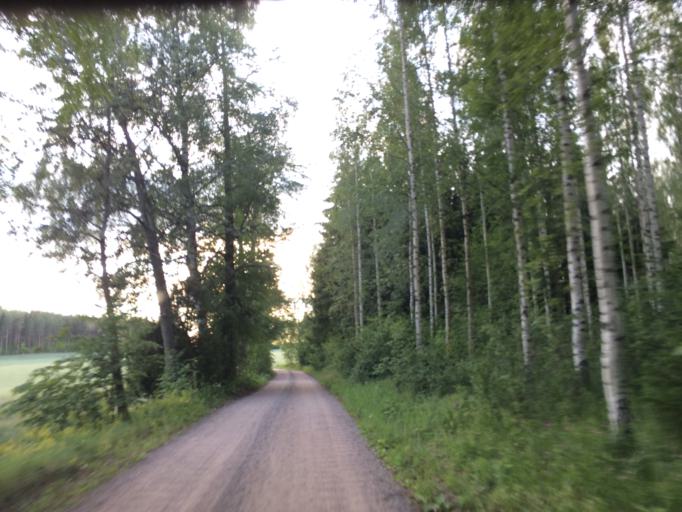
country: FI
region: Haeme
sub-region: Haemeenlinna
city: Janakkala
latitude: 60.8931
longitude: 24.6142
